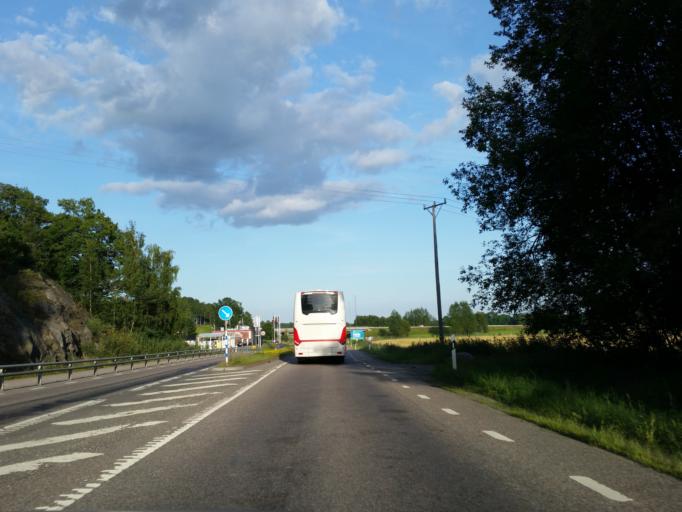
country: SE
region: Stockholm
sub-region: Sodertalje Kommun
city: Pershagen
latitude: 59.0871
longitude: 17.5907
